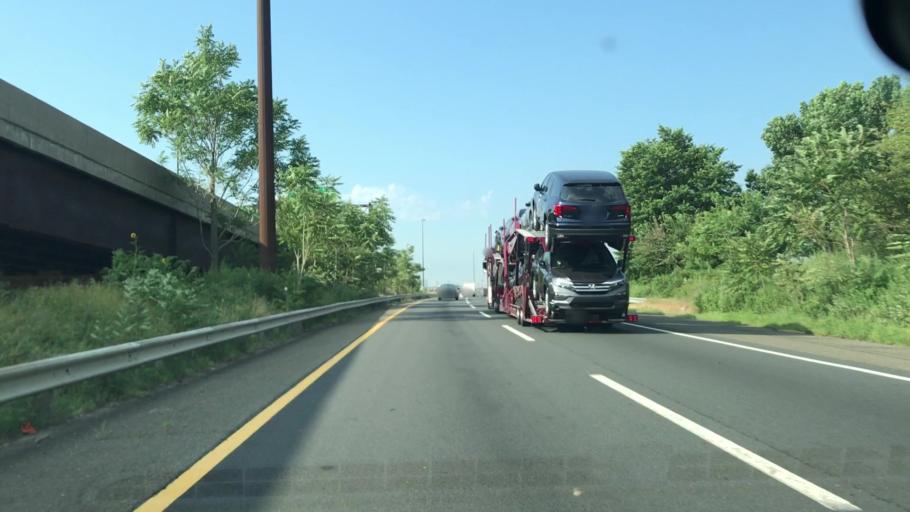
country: US
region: New Jersey
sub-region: Hudson County
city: Harrison
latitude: 40.7195
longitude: -74.1358
